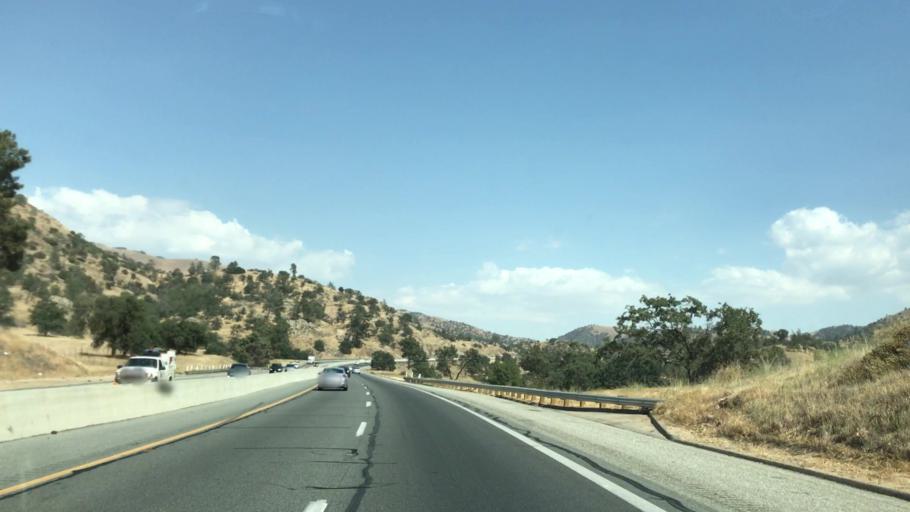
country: US
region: California
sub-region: Kern County
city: Golden Hills
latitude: 35.2093
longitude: -118.5401
